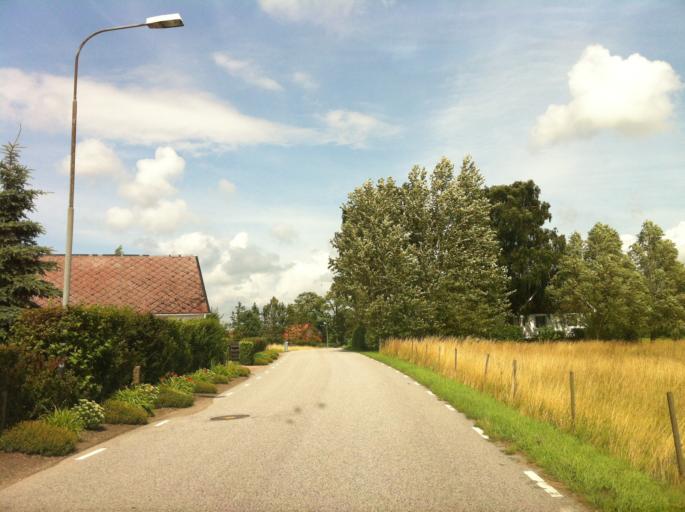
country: SE
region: Skane
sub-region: Skurups Kommun
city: Skurup
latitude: 55.4572
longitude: 13.4289
